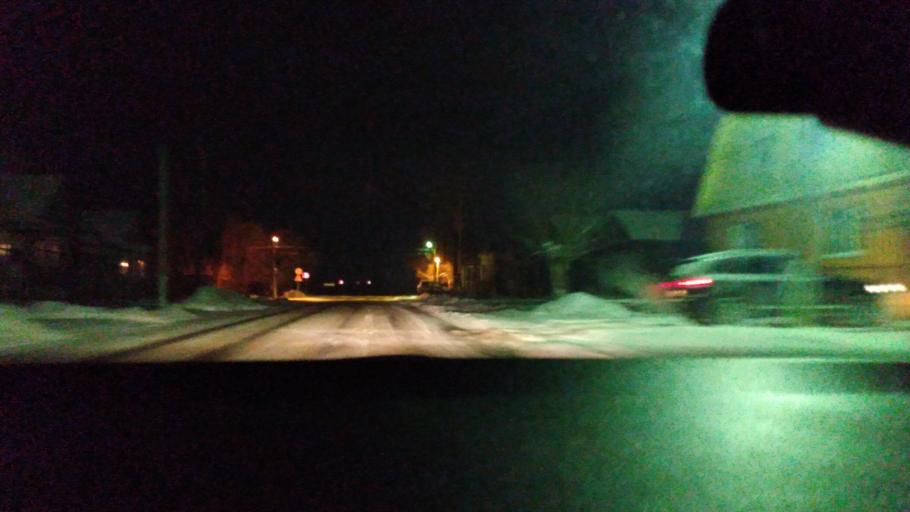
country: RU
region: Moskovskaya
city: Krasnaya Poyma
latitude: 55.0582
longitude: 39.1131
